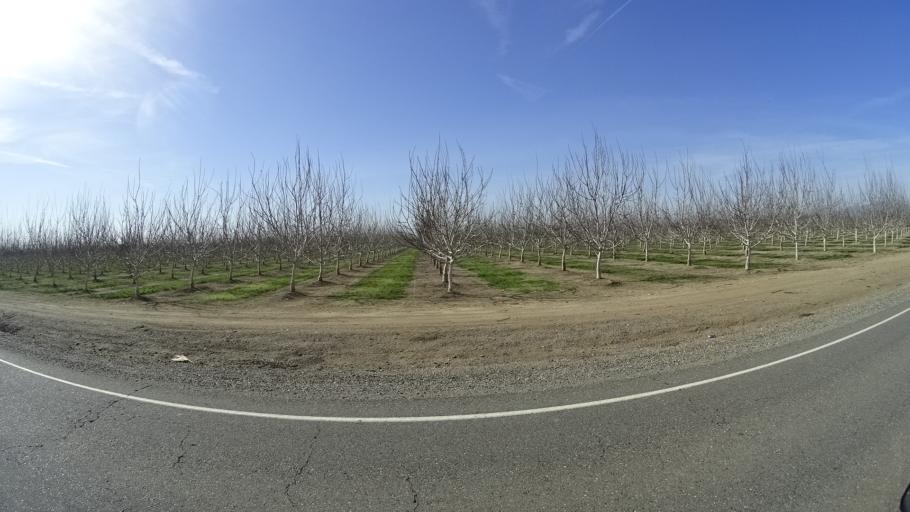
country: US
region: California
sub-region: Glenn County
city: Willows
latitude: 39.6245
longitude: -122.2219
